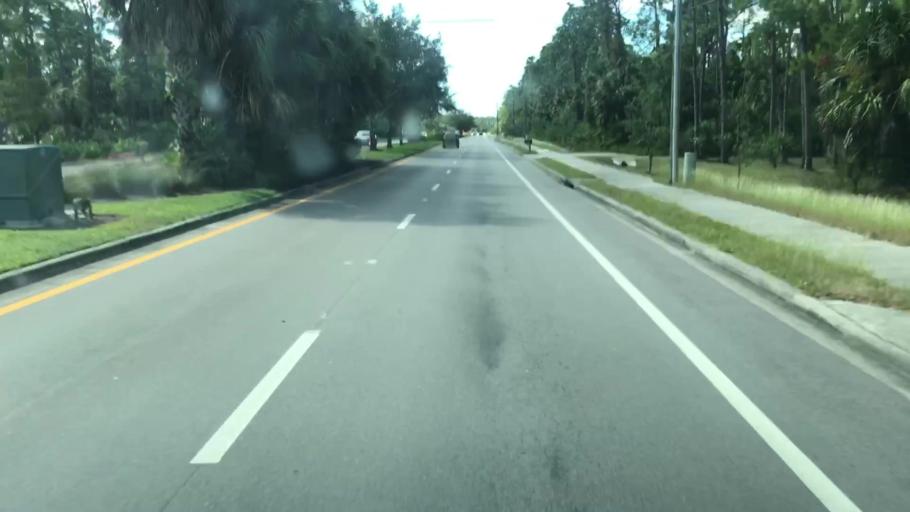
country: US
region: Florida
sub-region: Collier County
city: Vineyards
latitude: 26.2291
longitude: -81.6781
